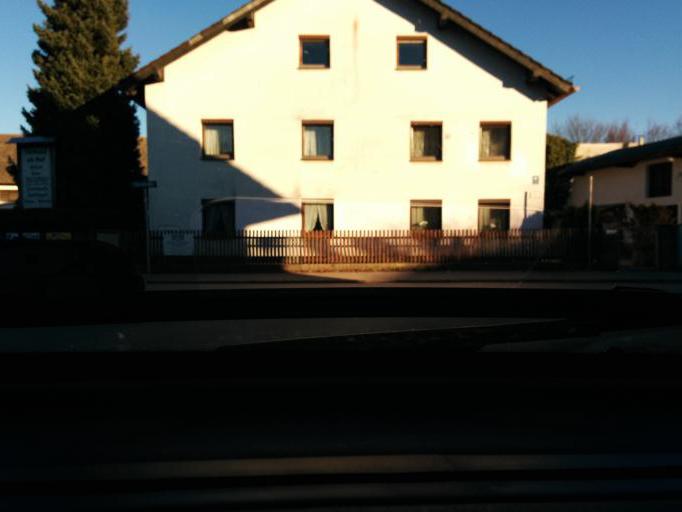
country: DE
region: Bavaria
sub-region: Upper Bavaria
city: Germering
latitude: 48.1612
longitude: 11.4124
